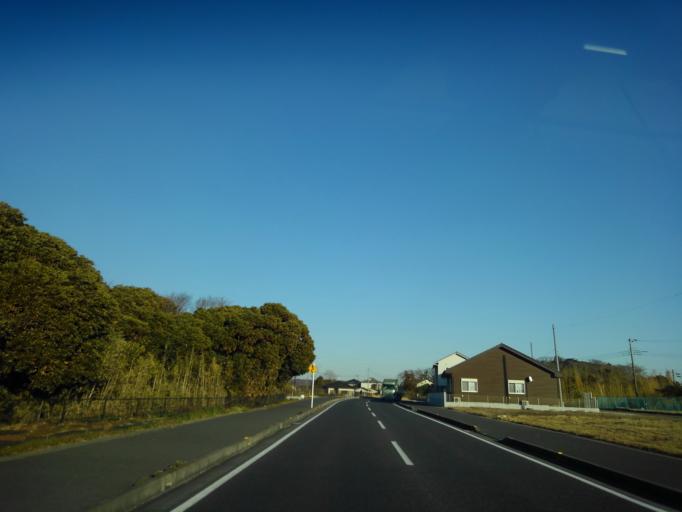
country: JP
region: Chiba
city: Kimitsu
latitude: 35.3231
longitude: 139.8960
